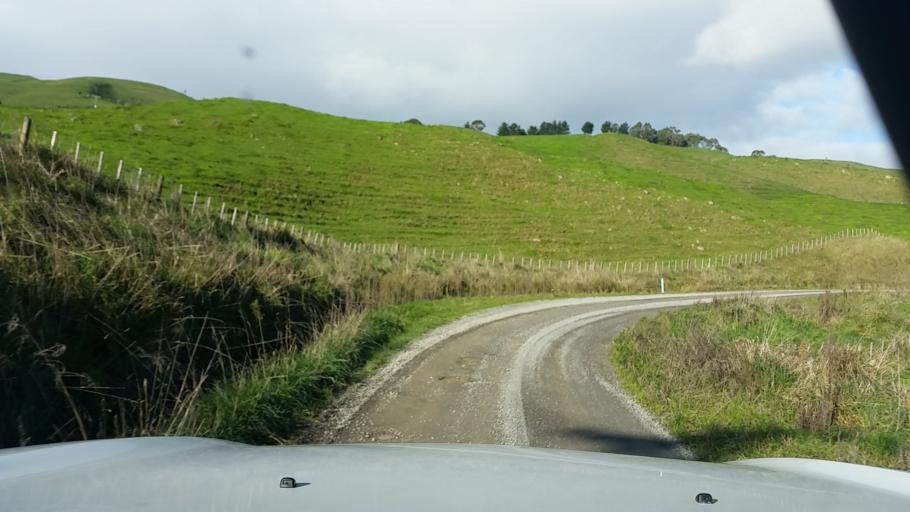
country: NZ
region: Wellington
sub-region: Masterton District
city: Masterton
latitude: -41.0474
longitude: 175.6948
